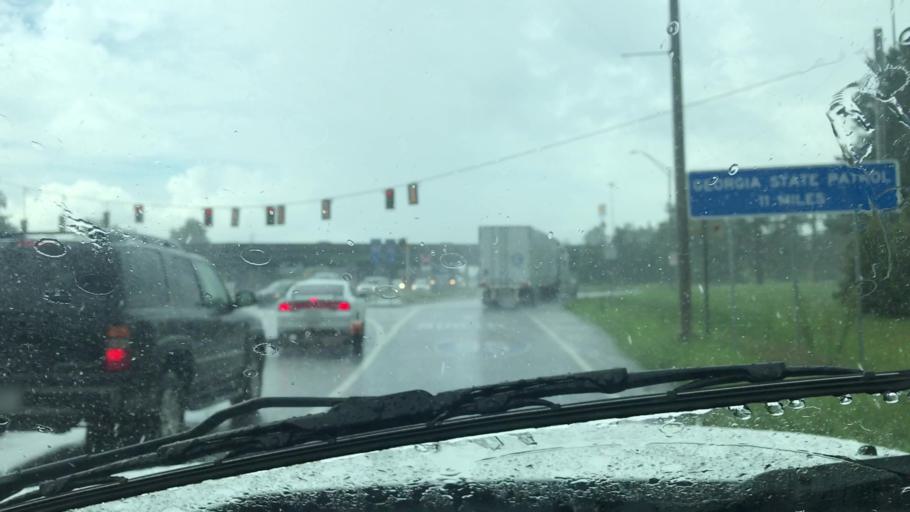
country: US
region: Georgia
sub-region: Chatham County
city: Port Wentworth
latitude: 32.1900
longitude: -81.1941
